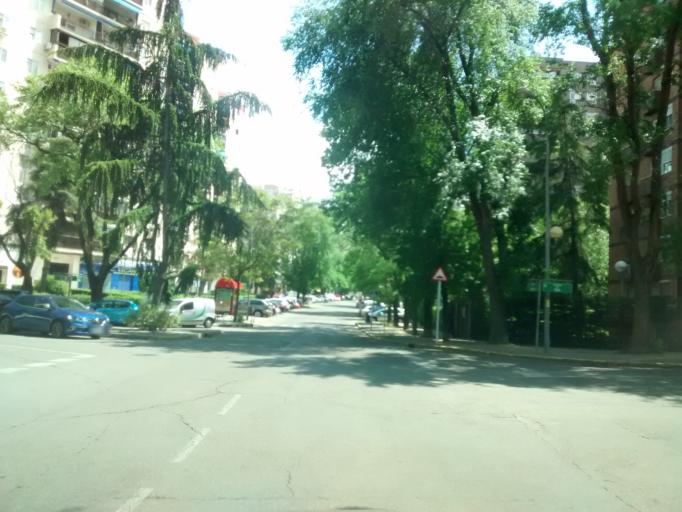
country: ES
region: Madrid
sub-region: Provincia de Madrid
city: San Fernando de Henares
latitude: 40.4302
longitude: -3.5418
